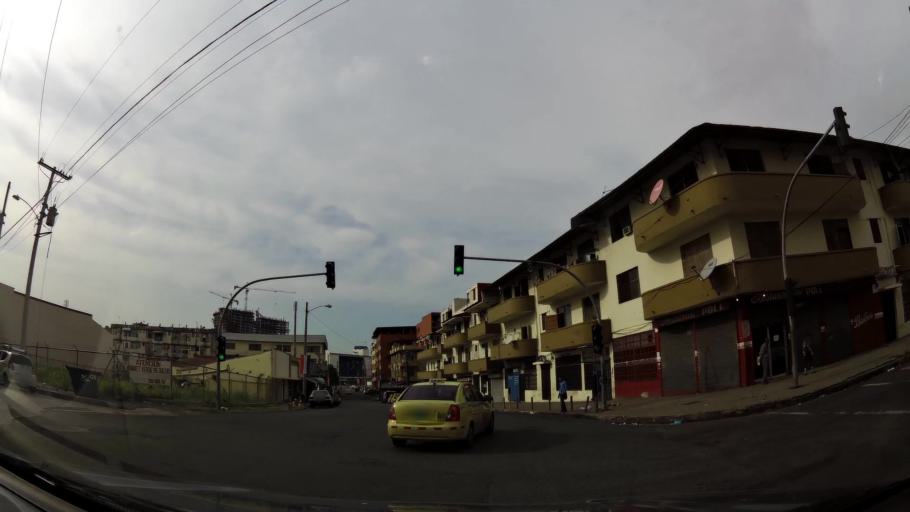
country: PA
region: Panama
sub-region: Distrito de Panama
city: Ancon
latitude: 8.9649
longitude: -79.5386
